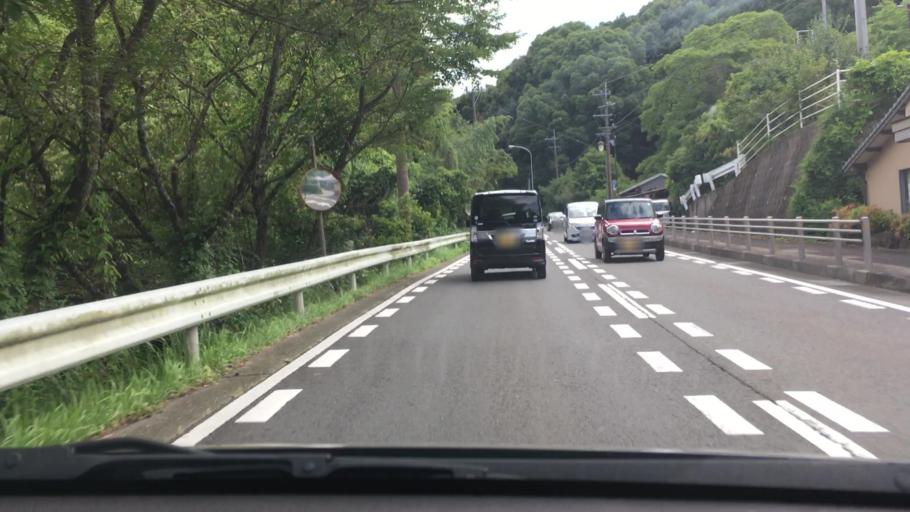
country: JP
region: Nagasaki
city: Togitsu
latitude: 32.9310
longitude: 129.7831
